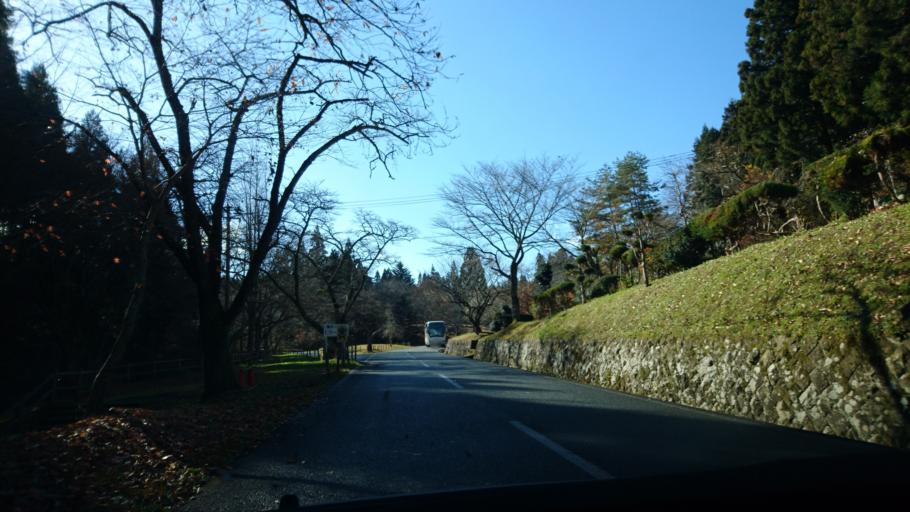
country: JP
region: Iwate
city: Ichinoseki
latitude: 38.9975
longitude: 141.0973
